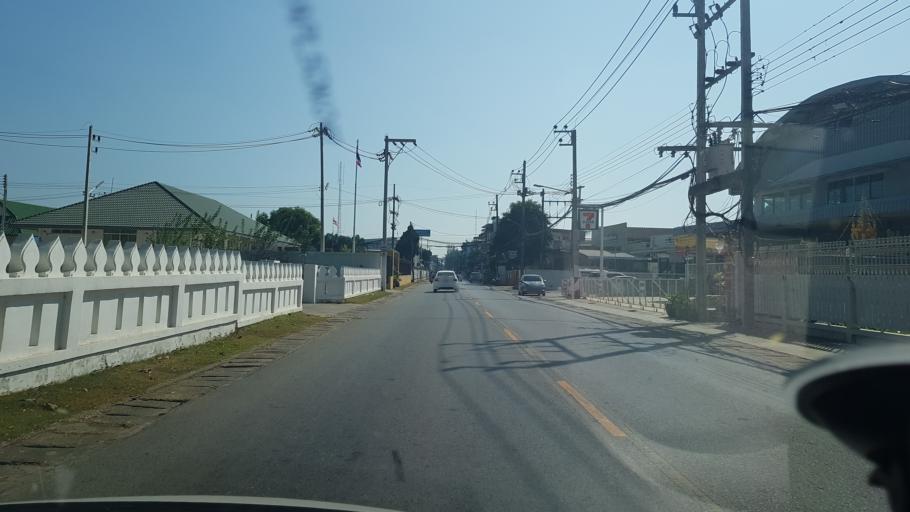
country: TH
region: Chiang Rai
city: Chiang Rai
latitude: 19.9044
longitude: 99.8119
